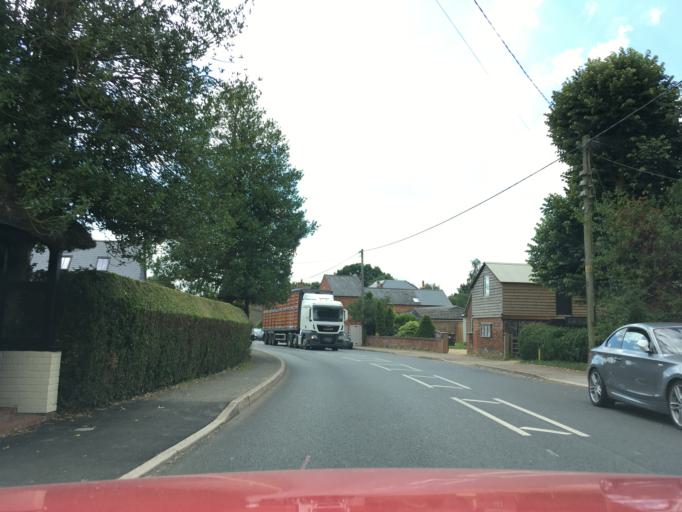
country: GB
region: England
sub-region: Buckinghamshire
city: Newton Longville
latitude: 51.9515
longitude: -0.8131
